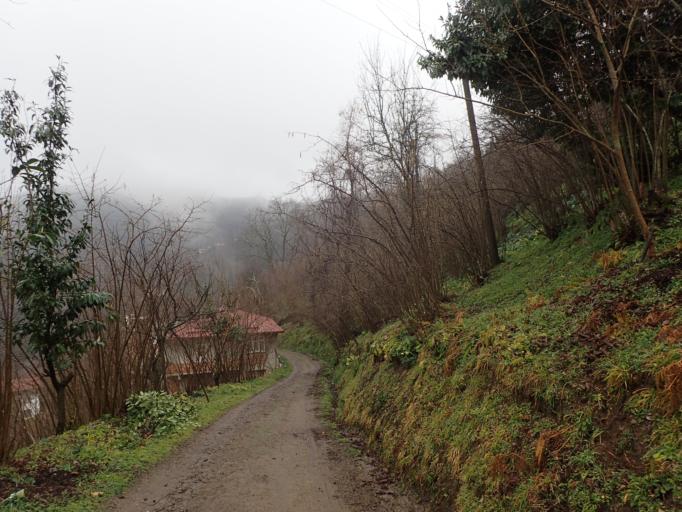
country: TR
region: Ordu
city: Camas
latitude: 40.9133
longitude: 37.5719
